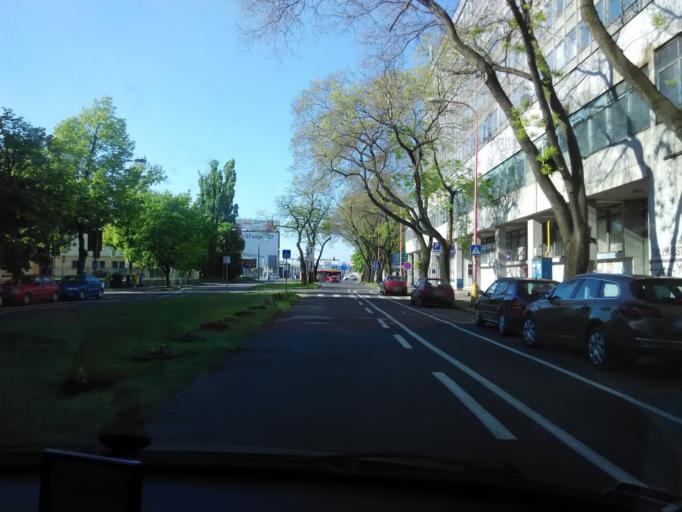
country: SK
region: Bratislavsky
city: Bratislava
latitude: 48.1473
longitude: 17.1329
